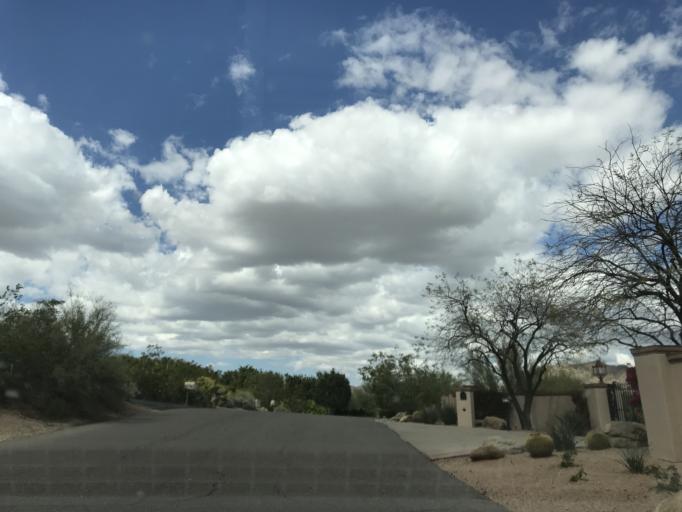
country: US
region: Arizona
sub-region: Maricopa County
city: Paradise Valley
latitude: 33.5192
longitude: -111.9527
